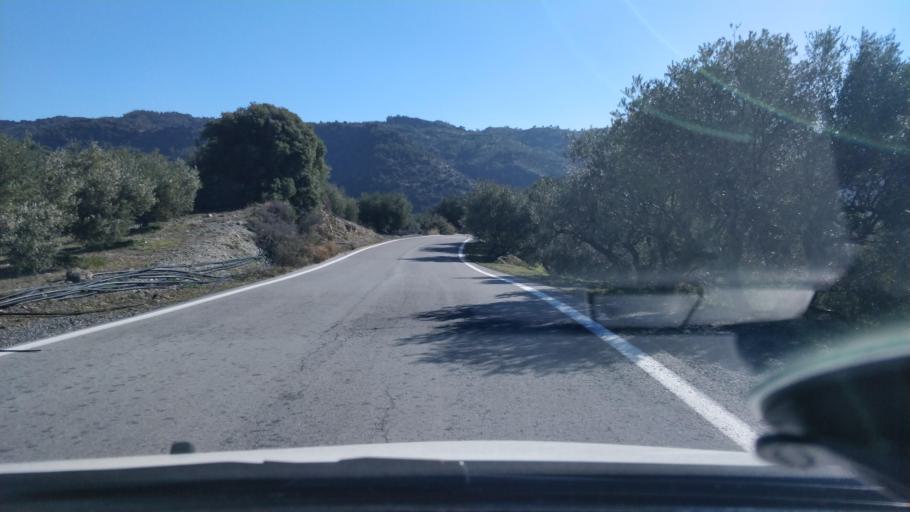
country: GR
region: Crete
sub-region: Nomos Irakleiou
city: Kastelli
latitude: 35.0315
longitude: 25.4478
